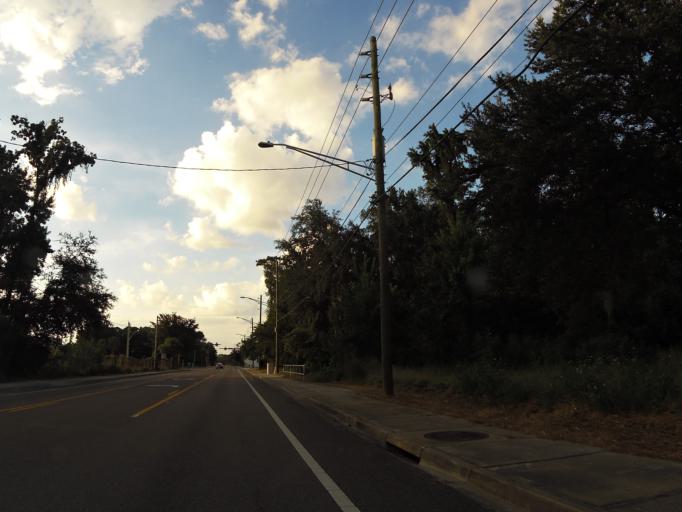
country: US
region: Florida
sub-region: Duval County
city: Jacksonville
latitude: 30.3351
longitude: -81.7055
